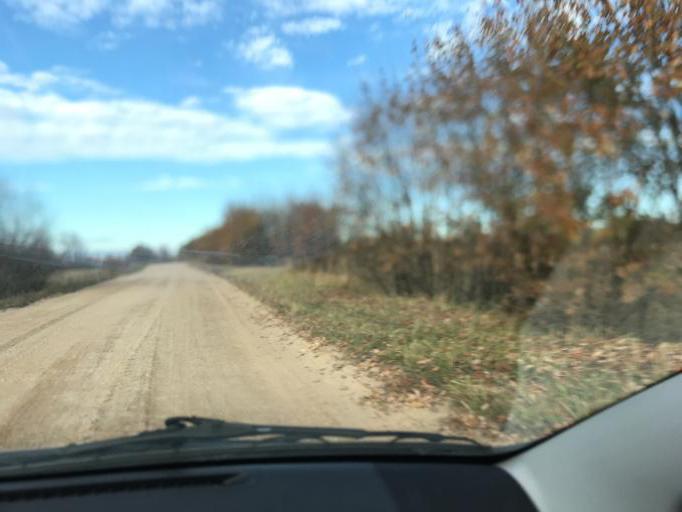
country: BY
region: Vitebsk
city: Haradok
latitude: 55.4531
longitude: 30.0255
